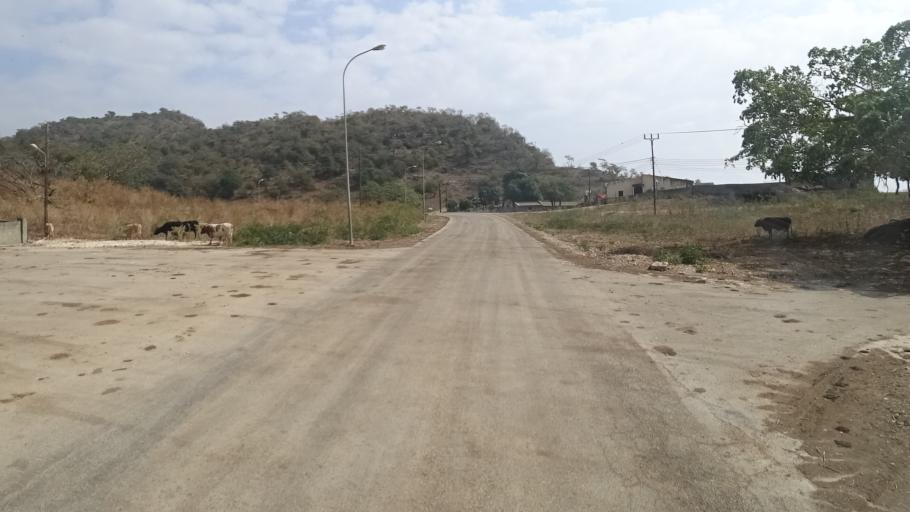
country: YE
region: Al Mahrah
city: Hawf
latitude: 16.7201
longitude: 53.2678
